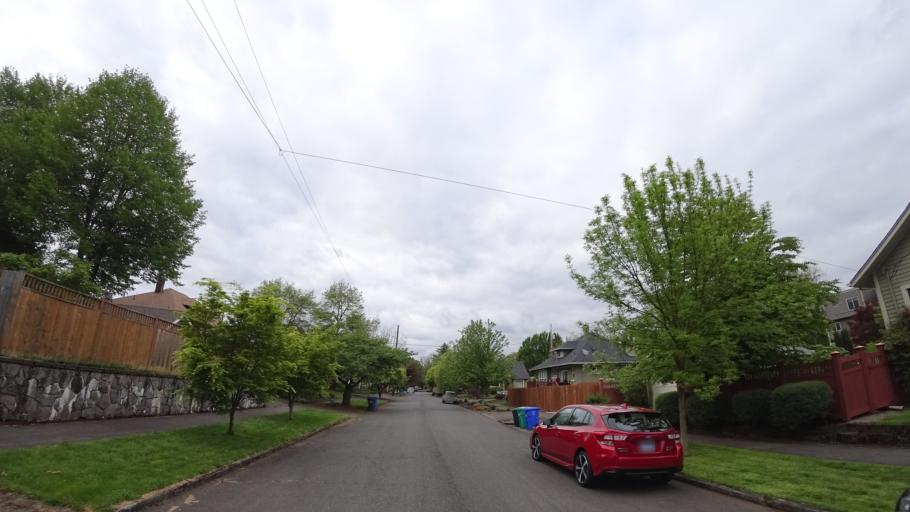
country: US
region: Oregon
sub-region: Clackamas County
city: Milwaukie
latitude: 45.4781
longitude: -122.6508
